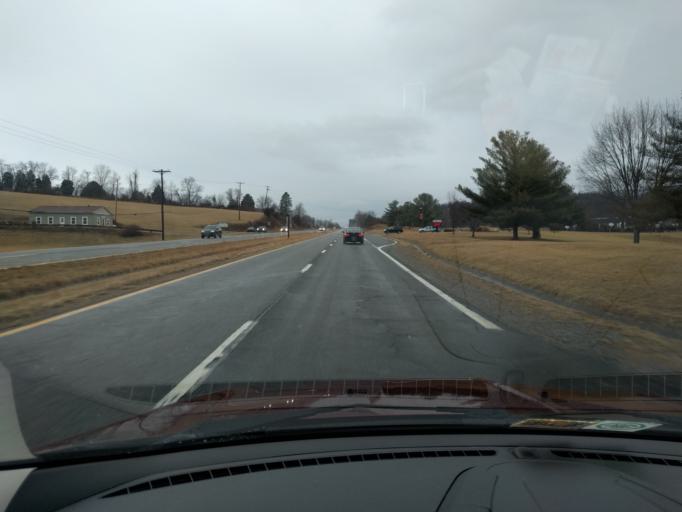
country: US
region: Virginia
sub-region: Giles County
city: Pembroke
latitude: 37.3115
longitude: -80.5806
